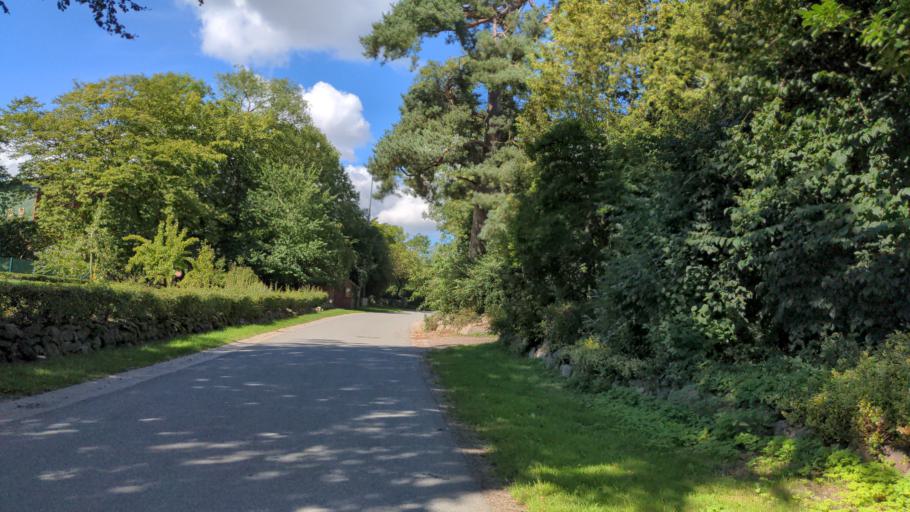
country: DE
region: Schleswig-Holstein
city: Beschendorf
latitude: 54.1778
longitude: 10.8420
